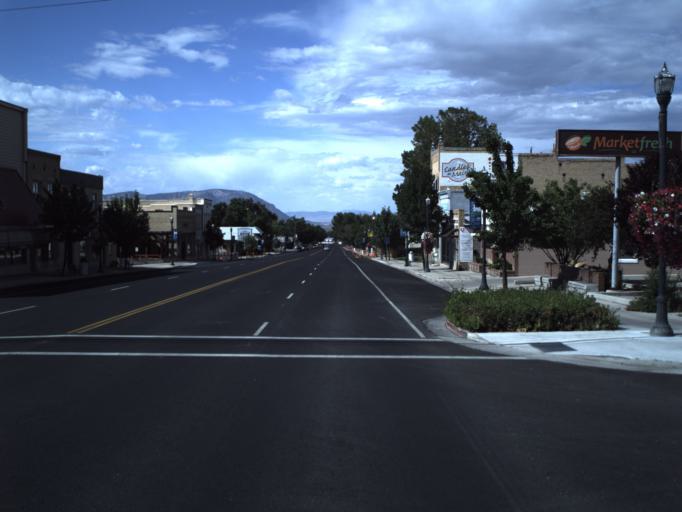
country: US
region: Utah
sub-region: Sanpete County
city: Manti
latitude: 39.2654
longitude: -111.6370
